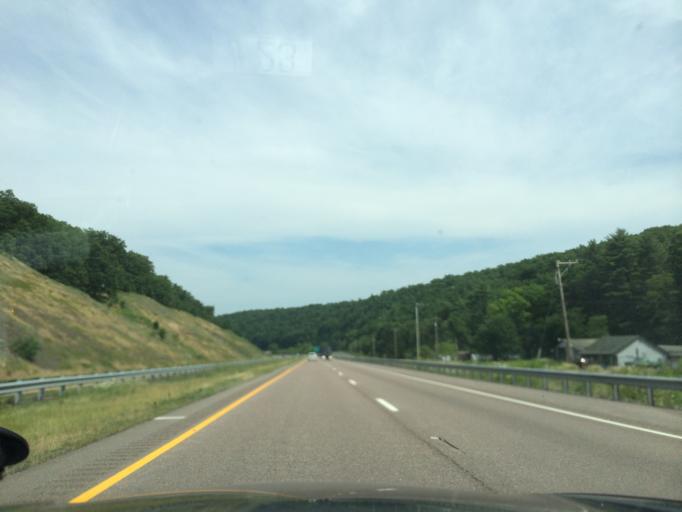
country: US
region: West Virginia
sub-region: Morgan County
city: Berkeley Springs
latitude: 39.6797
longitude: -78.4791
